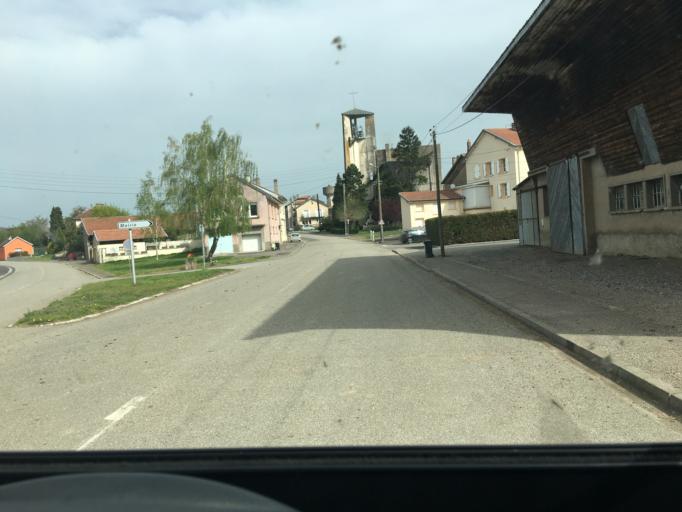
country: FR
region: Lorraine
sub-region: Departement de la Moselle
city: Vic-sur-Seille
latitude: 48.7767
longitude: 6.5629
